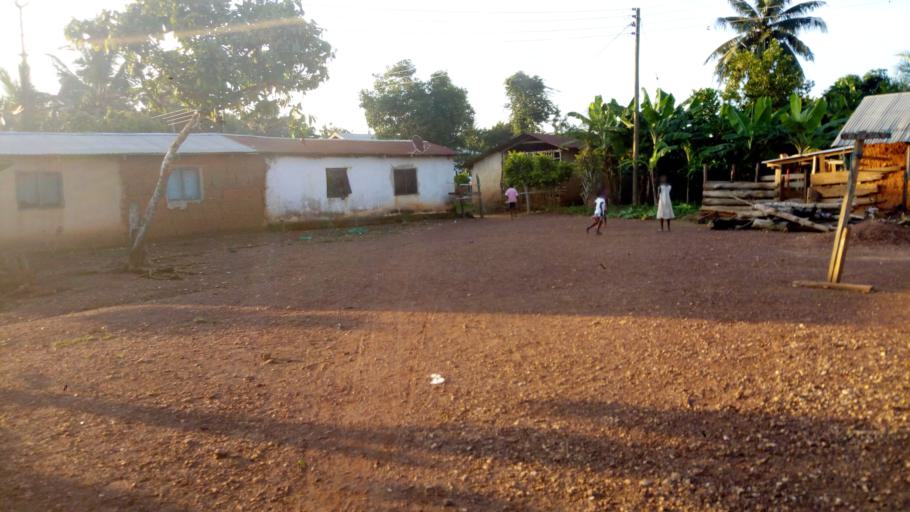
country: GH
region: Eastern
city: Akwatia
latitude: 6.1598
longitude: -0.8153
